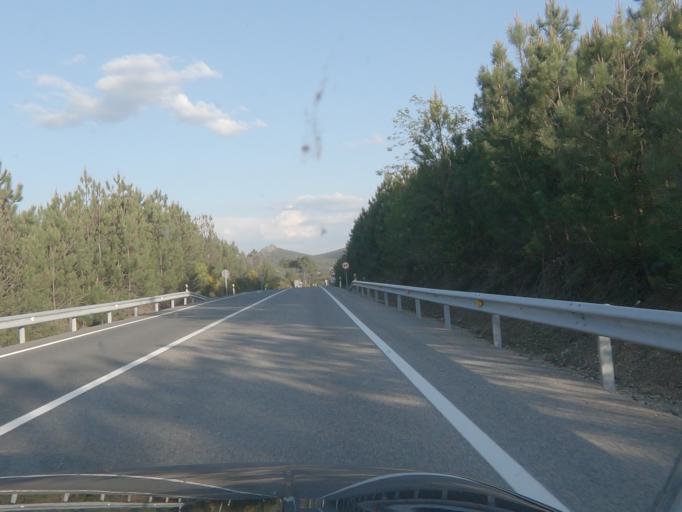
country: PT
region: Portalegre
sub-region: Portalegre
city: Sao Juliao
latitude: 39.3488
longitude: -7.3022
